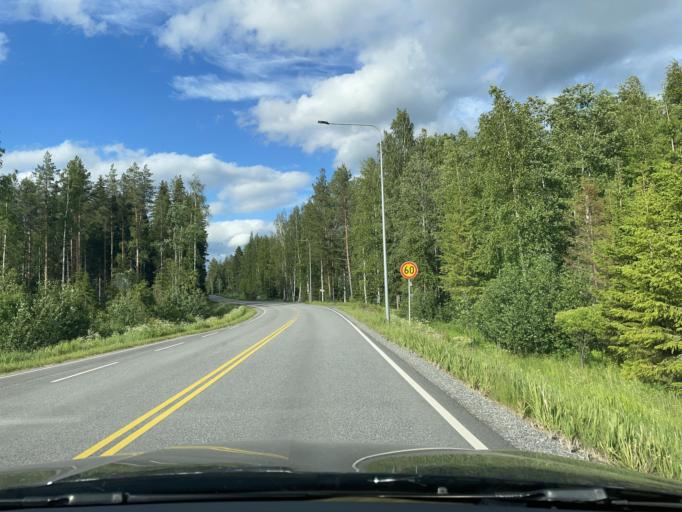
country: FI
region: Central Finland
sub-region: Jaemsae
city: Jaemsaenkoski
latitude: 62.0699
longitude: 25.1373
